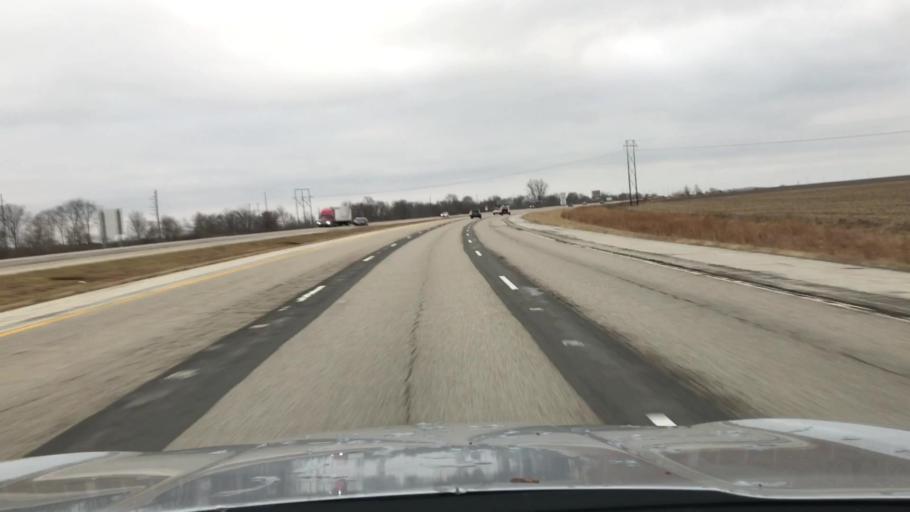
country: US
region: Illinois
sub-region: Logan County
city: Lincoln
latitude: 40.1028
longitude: -89.4166
